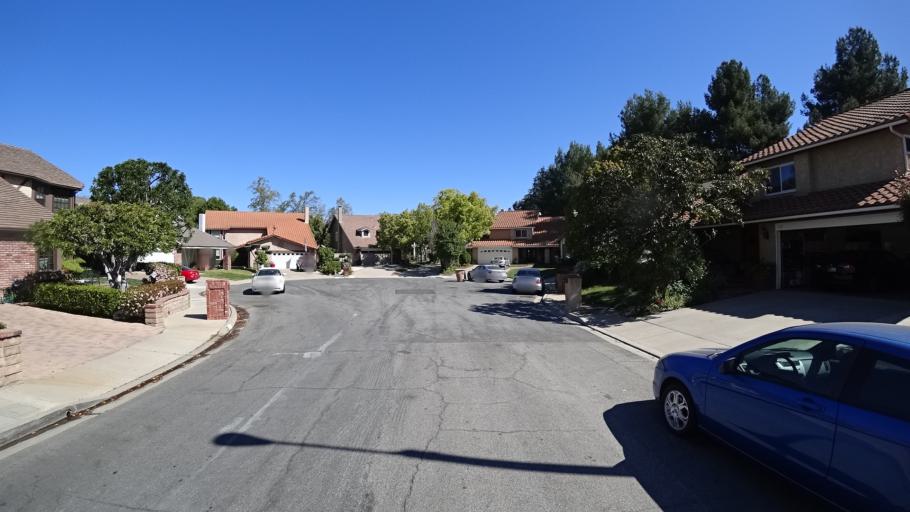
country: US
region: California
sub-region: Ventura County
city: Thousand Oaks
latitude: 34.1745
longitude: -118.8755
